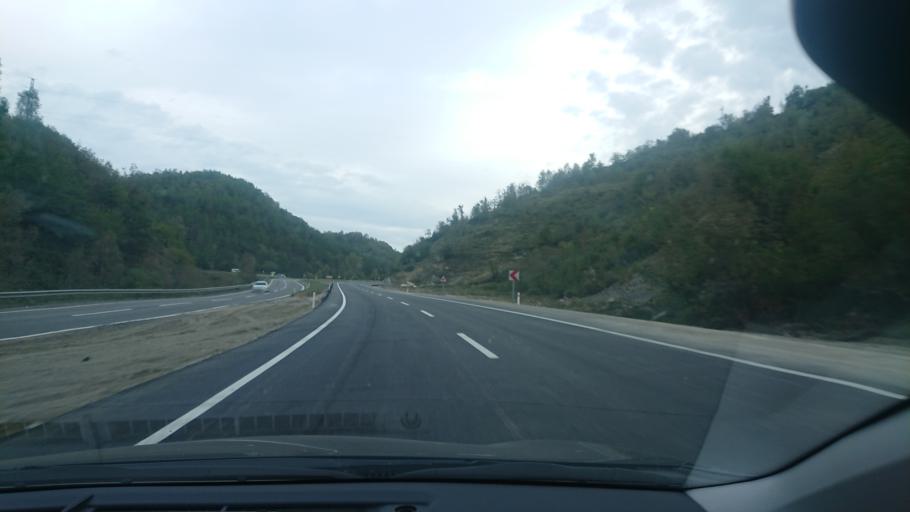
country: TR
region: Zonguldak
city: Beycuma
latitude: 41.3942
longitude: 31.9366
